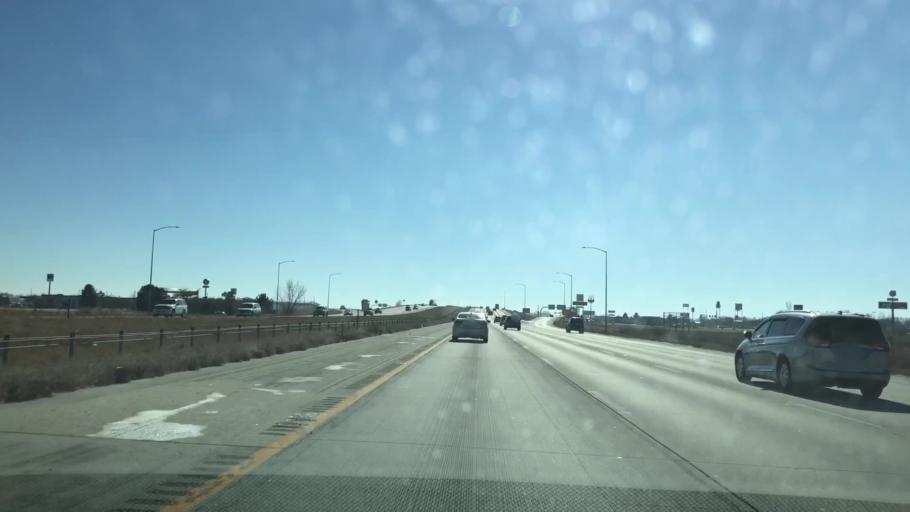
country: US
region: Colorado
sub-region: Weld County
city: Firestone
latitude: 40.1660
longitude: -104.9797
